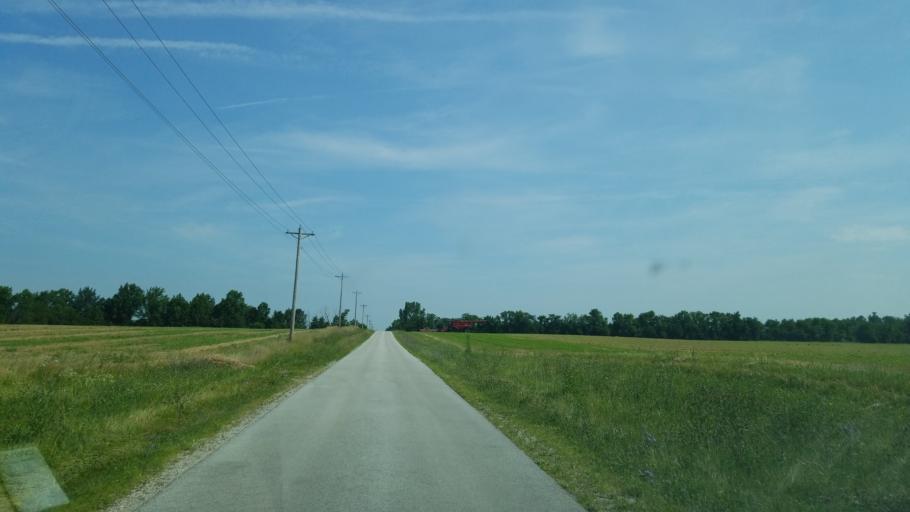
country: US
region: Ohio
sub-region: Sandusky County
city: Green Springs
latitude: 41.1286
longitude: -82.9961
